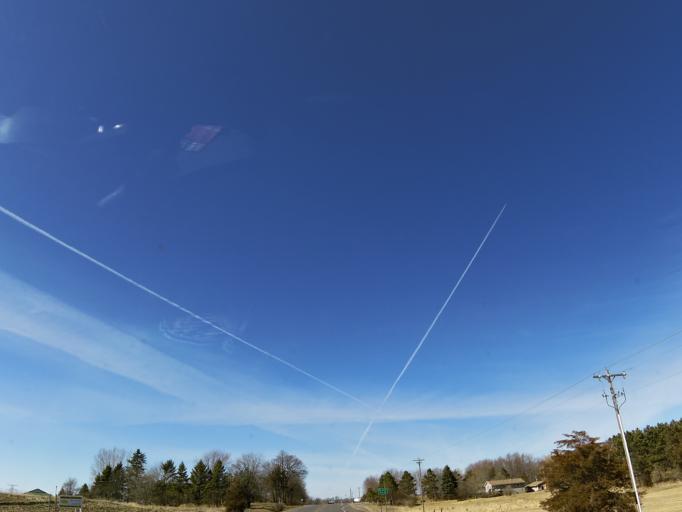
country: US
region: Minnesota
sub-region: Wright County
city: Rockford
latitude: 45.1157
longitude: -93.7969
